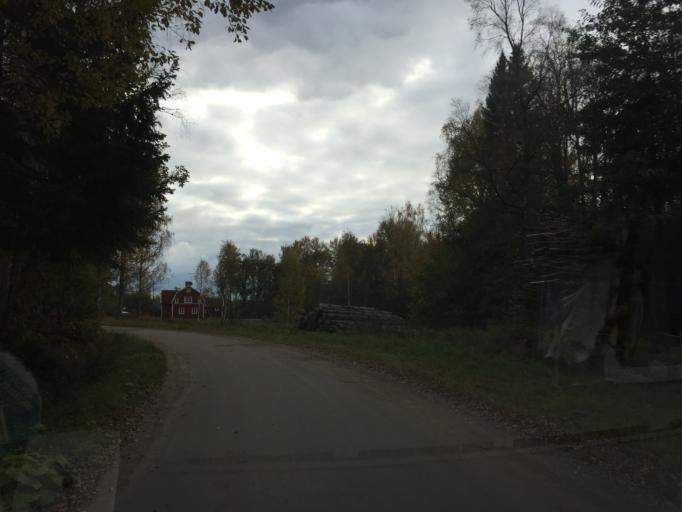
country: SE
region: Soedermanland
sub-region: Vingakers Kommun
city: Vingaker
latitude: 59.0148
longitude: 15.7784
